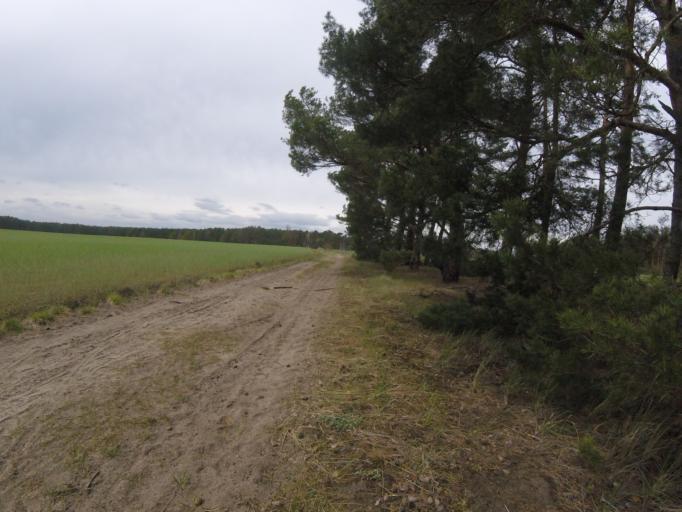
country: DE
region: Brandenburg
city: Bestensee
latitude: 52.2191
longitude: 13.6750
